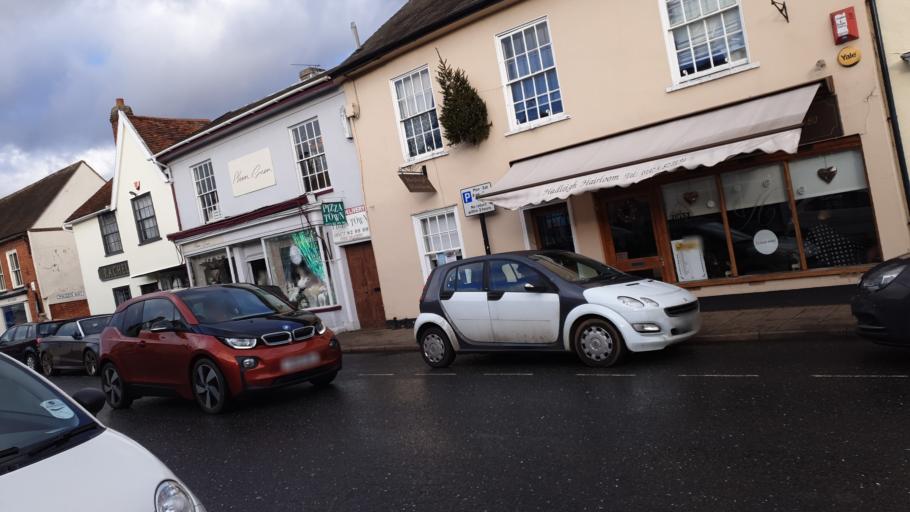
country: GB
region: England
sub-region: Suffolk
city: Hadleigh
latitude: 52.0444
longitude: 0.9534
